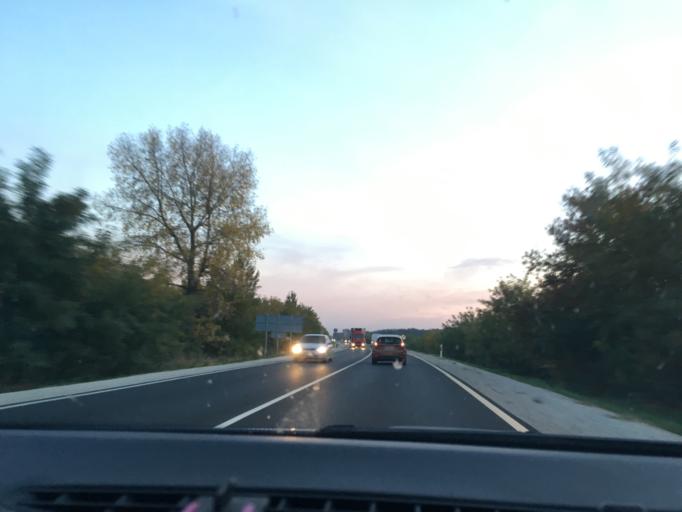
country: HU
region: Hajdu-Bihar
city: Debrecen
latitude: 47.5972
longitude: 21.6535
